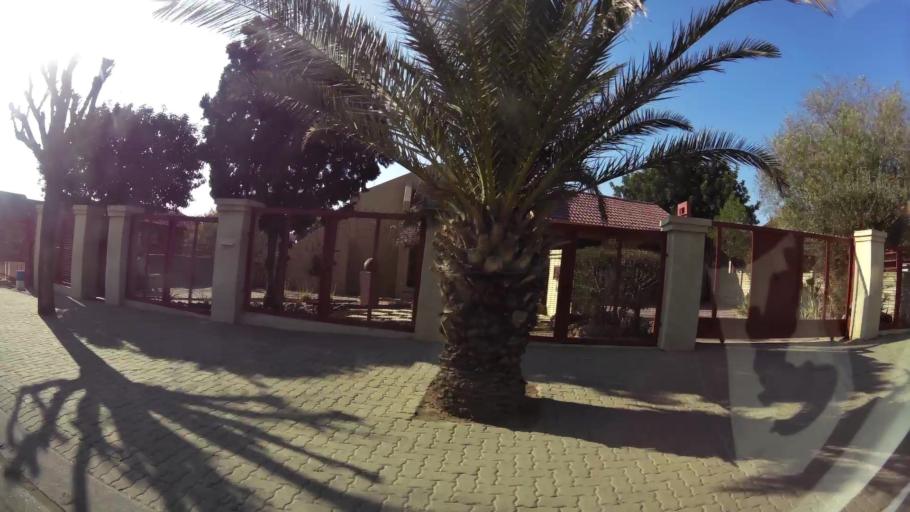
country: ZA
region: Orange Free State
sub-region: Mangaung Metropolitan Municipality
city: Bloemfontein
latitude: -29.1862
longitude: 26.2225
